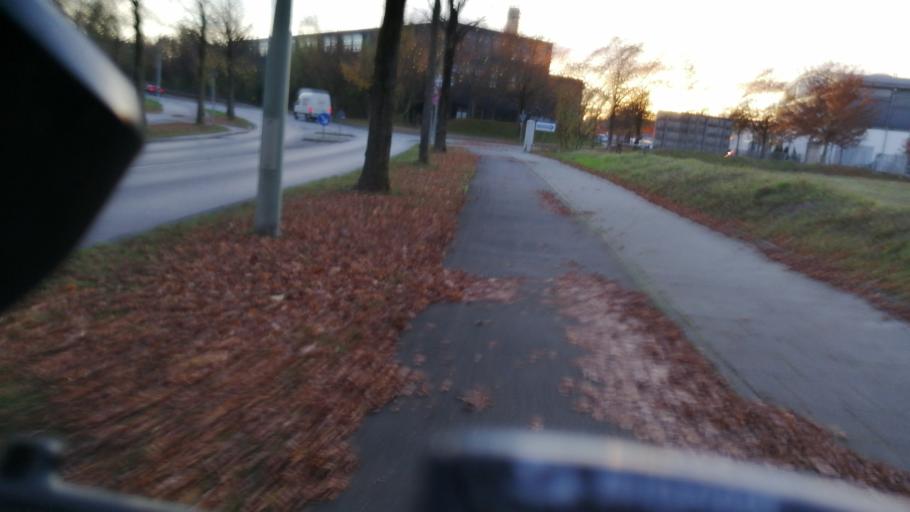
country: DE
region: Bavaria
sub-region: Upper Bavaria
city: Unterfoehring
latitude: 48.1925
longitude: 11.6026
